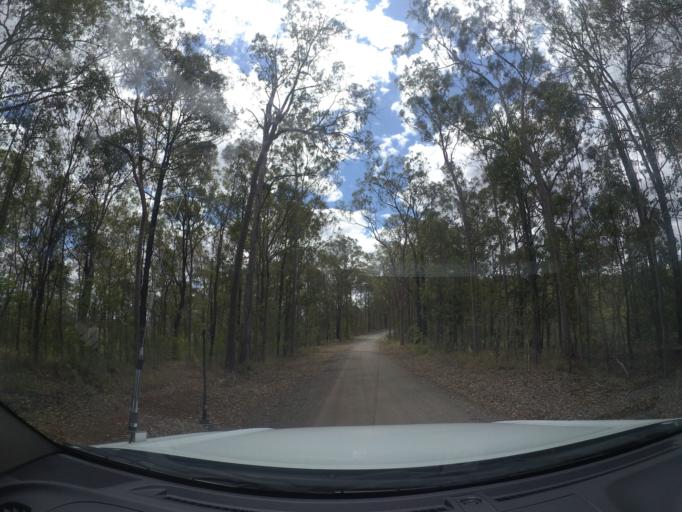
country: AU
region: Queensland
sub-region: Logan
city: Cedar Vale
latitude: -27.9089
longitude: 153.0311
